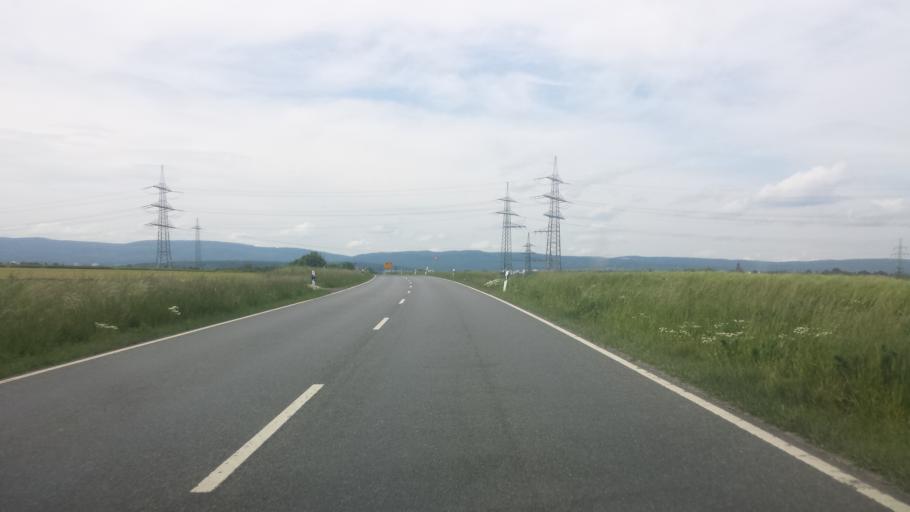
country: DE
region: Hesse
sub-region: Regierungsbezirk Darmstadt
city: Bad Vilbel
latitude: 50.2164
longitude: 8.6921
